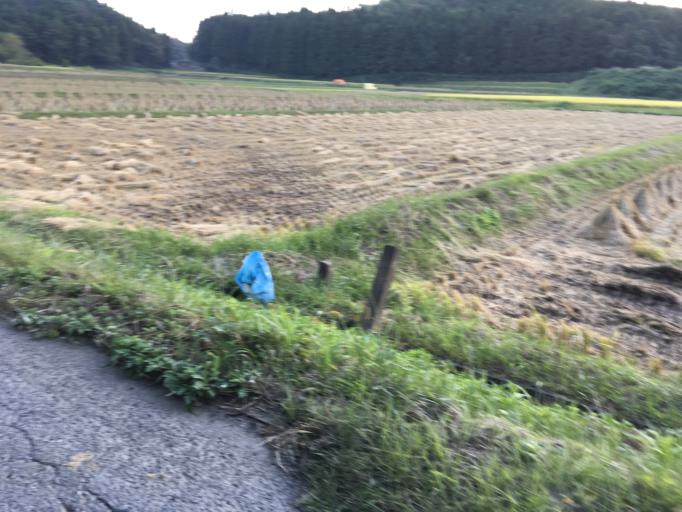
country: JP
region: Iwate
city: Ichinoseki
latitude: 38.7837
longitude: 141.2415
